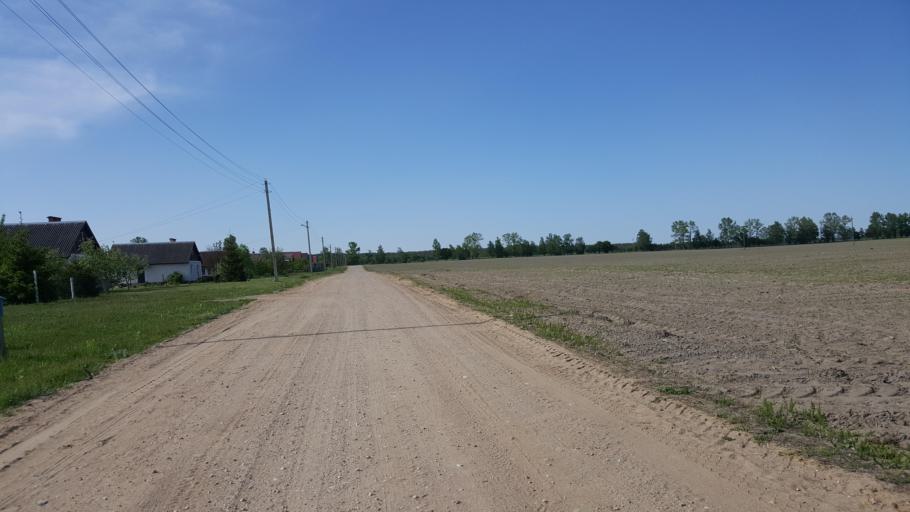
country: BY
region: Brest
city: Kamyanyets
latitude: 52.3335
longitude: 23.7845
